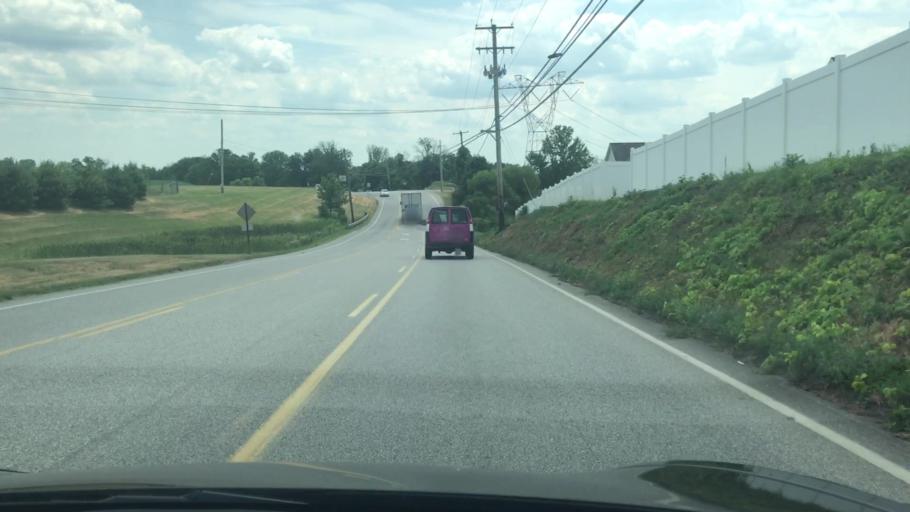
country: US
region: Pennsylvania
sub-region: York County
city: Manchester
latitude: 40.0671
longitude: -76.7673
